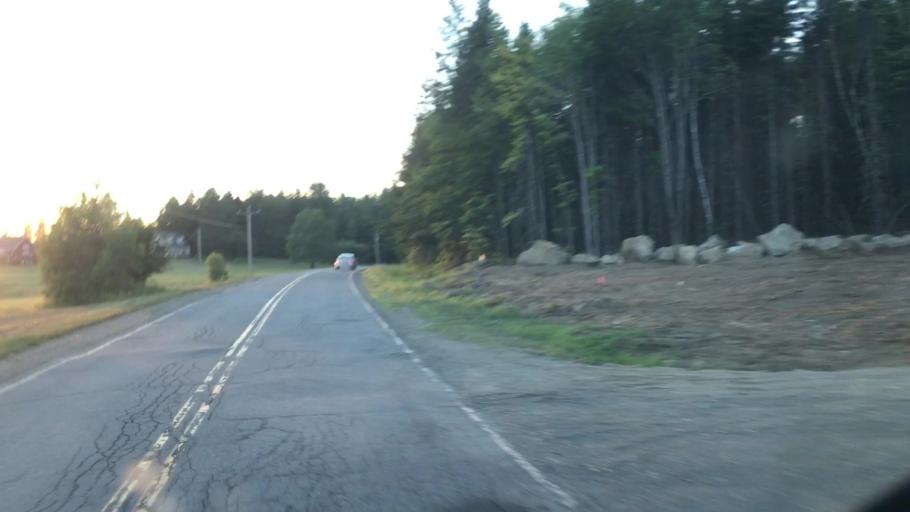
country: US
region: Maine
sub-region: Penobscot County
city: Medway
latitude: 45.6058
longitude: -68.2548
